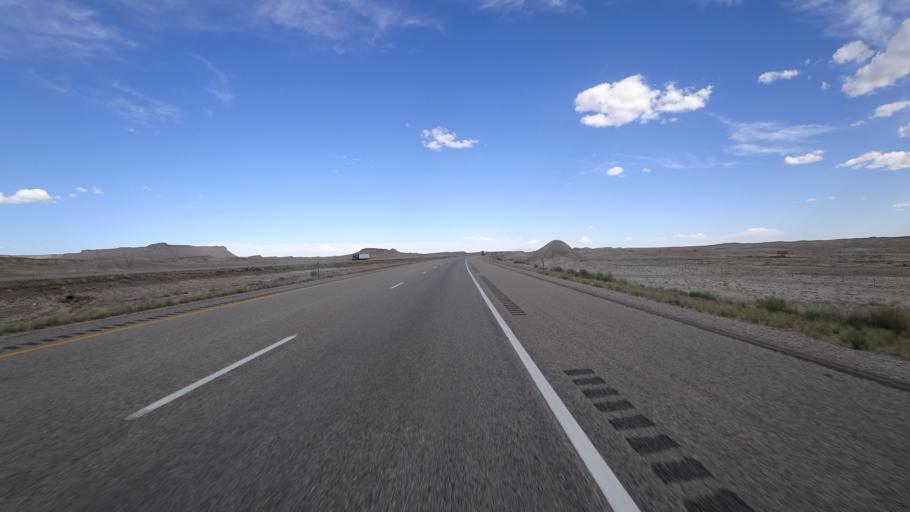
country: US
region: Utah
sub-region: Grand County
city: Moab
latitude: 38.9322
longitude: -110.0172
